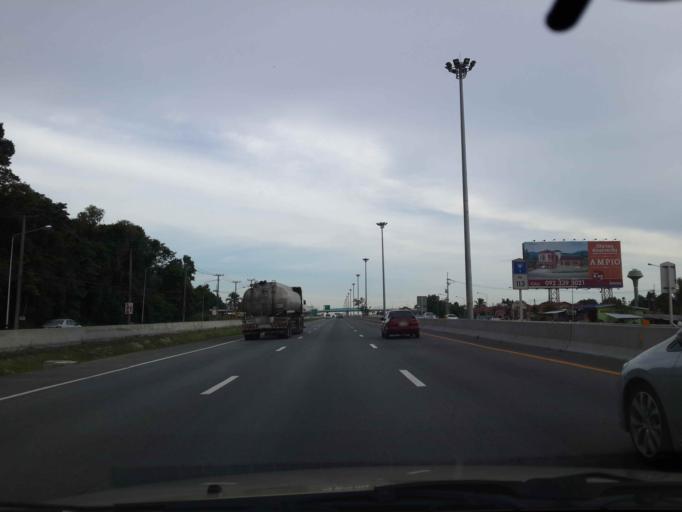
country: TH
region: Chon Buri
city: Ban Talat Bueng
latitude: 12.9995
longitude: 100.9923
